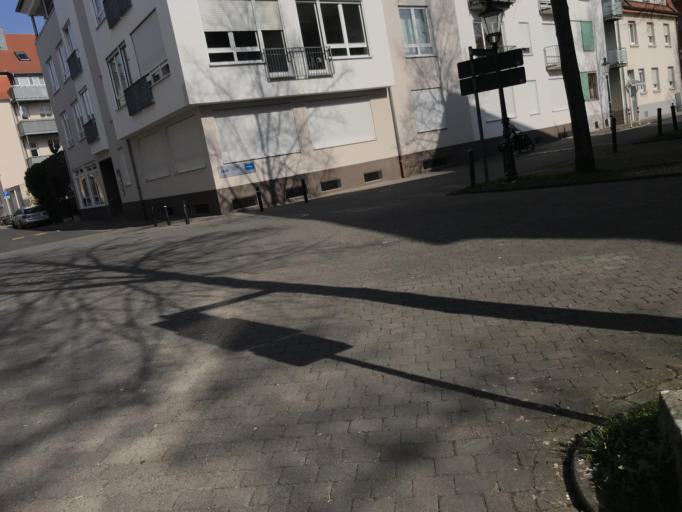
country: DE
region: Hesse
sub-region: Regierungsbezirk Kassel
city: Fulda
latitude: 50.5521
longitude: 9.6697
